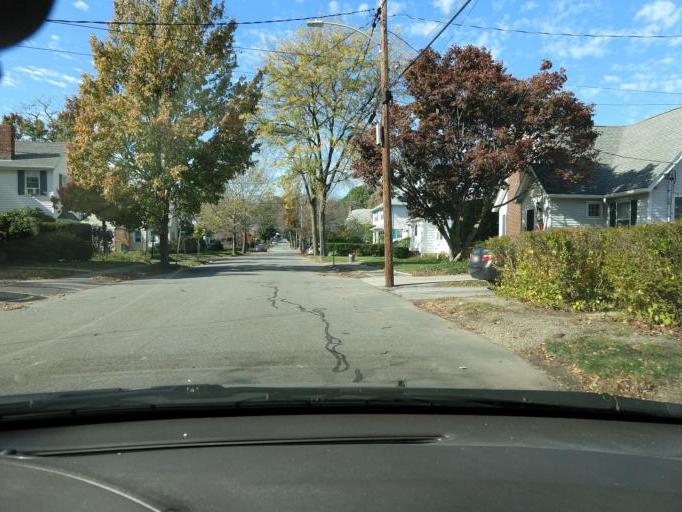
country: US
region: Massachusetts
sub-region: Middlesex County
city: Belmont
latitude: 42.3973
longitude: -71.1713
